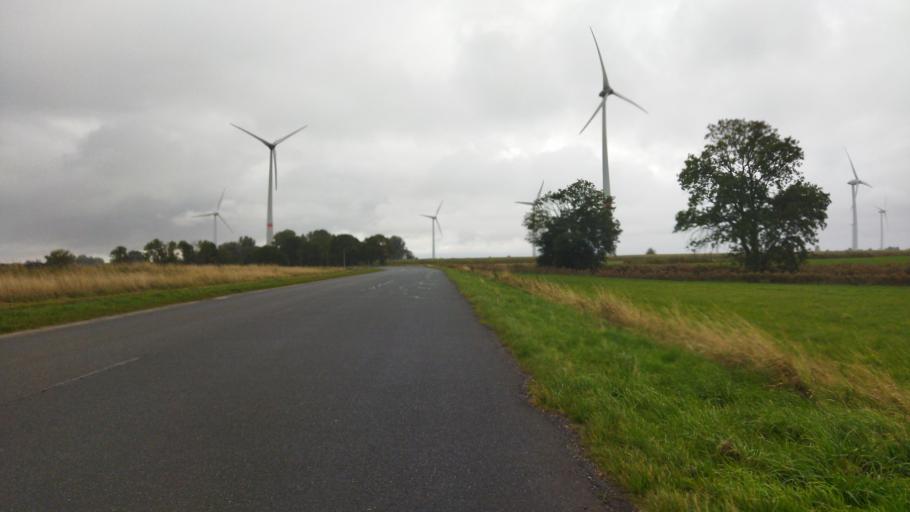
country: DE
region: Lower Saxony
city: Emden
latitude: 53.3443
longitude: 7.1379
